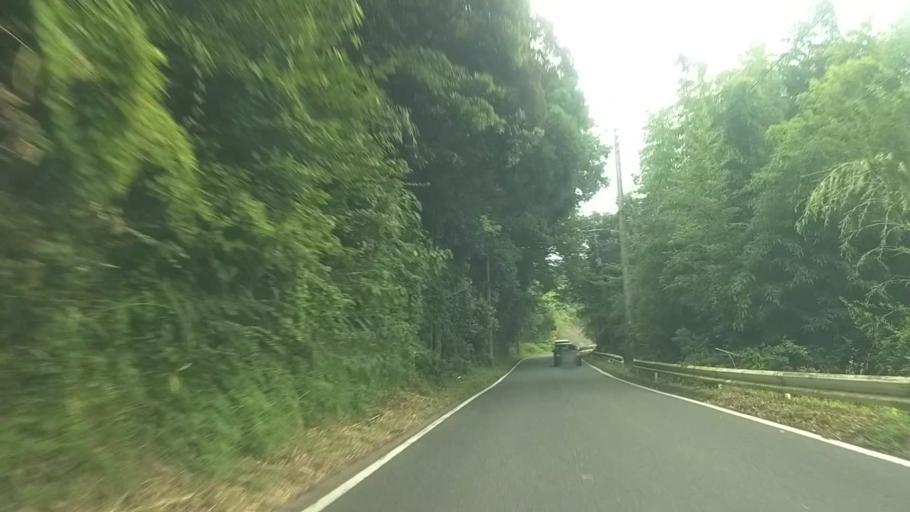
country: JP
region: Chiba
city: Kimitsu
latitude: 35.2387
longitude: 140.0011
